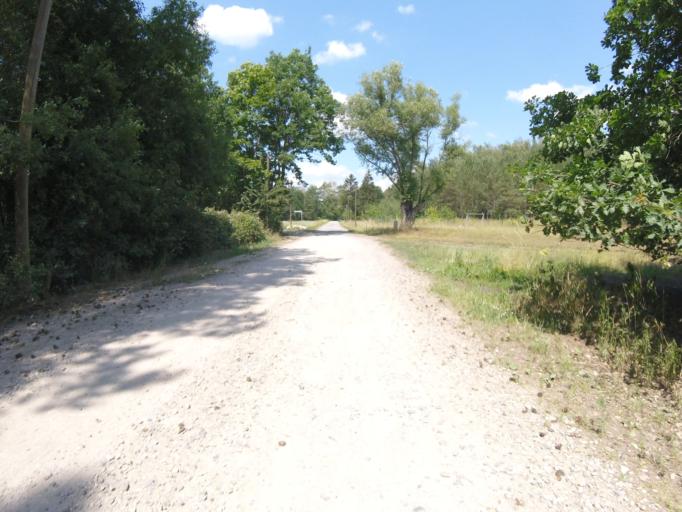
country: DE
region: Brandenburg
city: Bestensee
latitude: 52.2459
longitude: 13.6923
